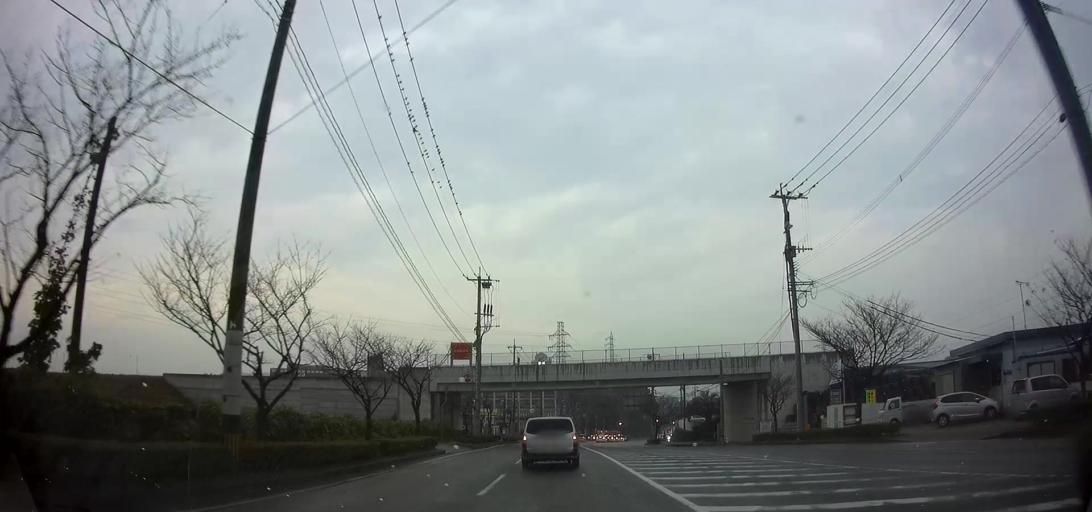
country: JP
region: Nagasaki
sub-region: Isahaya-shi
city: Isahaya
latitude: 32.8384
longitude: 130.0138
